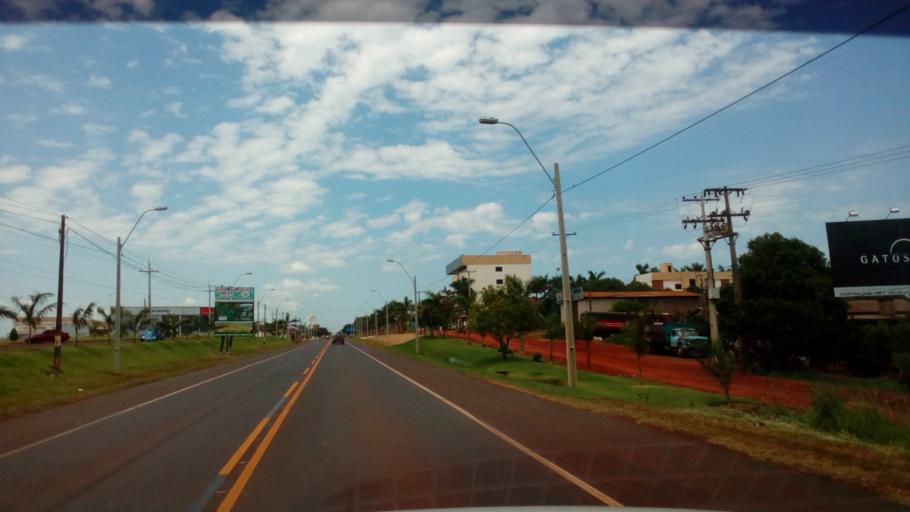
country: PY
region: Alto Parana
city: Santa Rita
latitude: -25.7698
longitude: -55.0699
